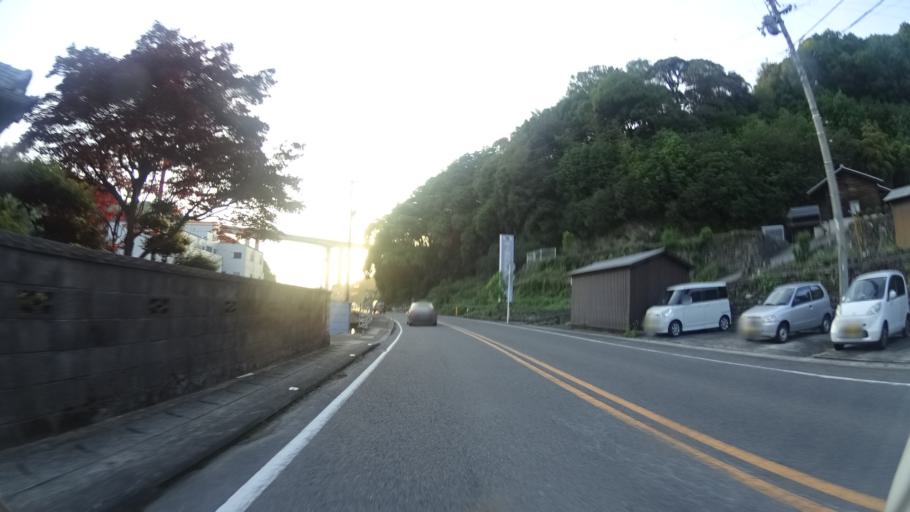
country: JP
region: Ehime
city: Kawanoecho
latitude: 33.9917
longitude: 133.6241
